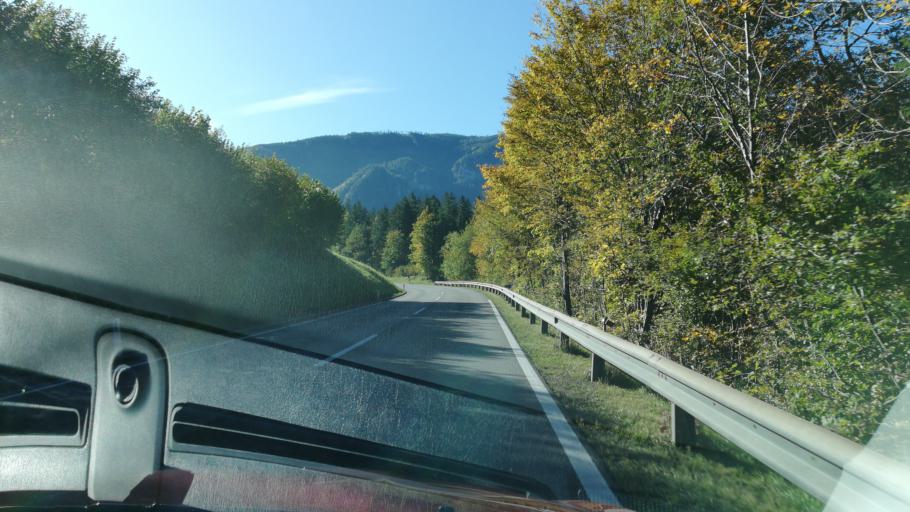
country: AT
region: Upper Austria
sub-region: Politischer Bezirk Steyr-Land
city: Weyer
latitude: 47.8658
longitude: 14.6097
